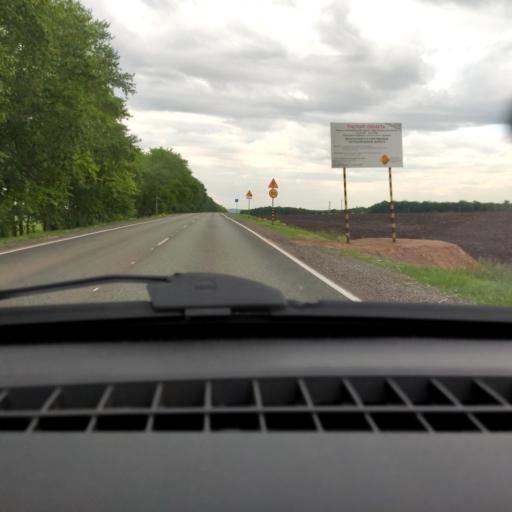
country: RU
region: Bashkortostan
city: Chishmy
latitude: 54.5721
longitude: 55.5561
